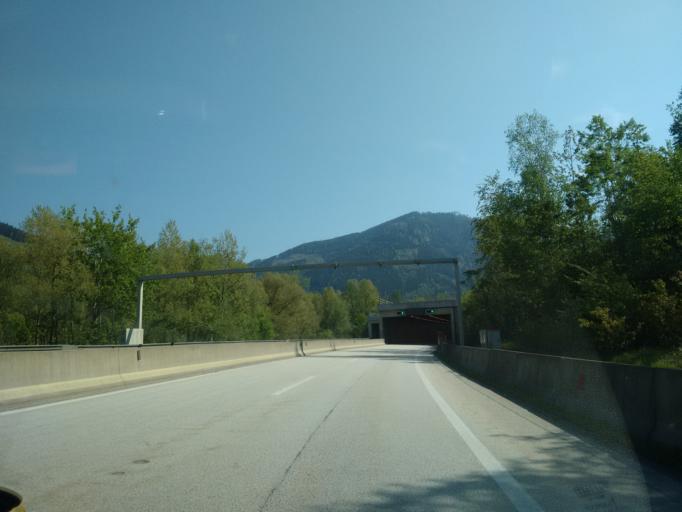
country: AT
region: Styria
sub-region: Politischer Bezirk Bruck-Muerzzuschlag
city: Oberaich
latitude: 47.4059
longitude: 15.1954
